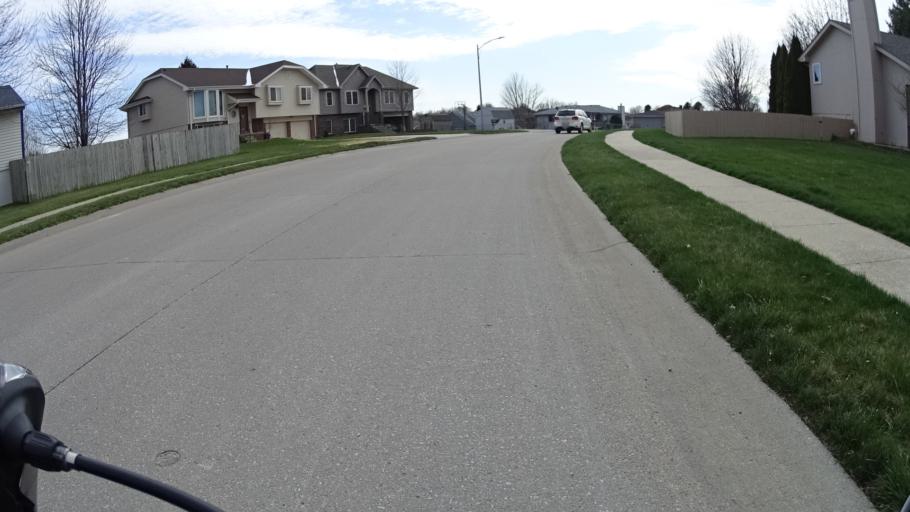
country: US
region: Nebraska
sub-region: Sarpy County
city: Offutt Air Force Base
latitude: 41.1117
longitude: -95.9600
